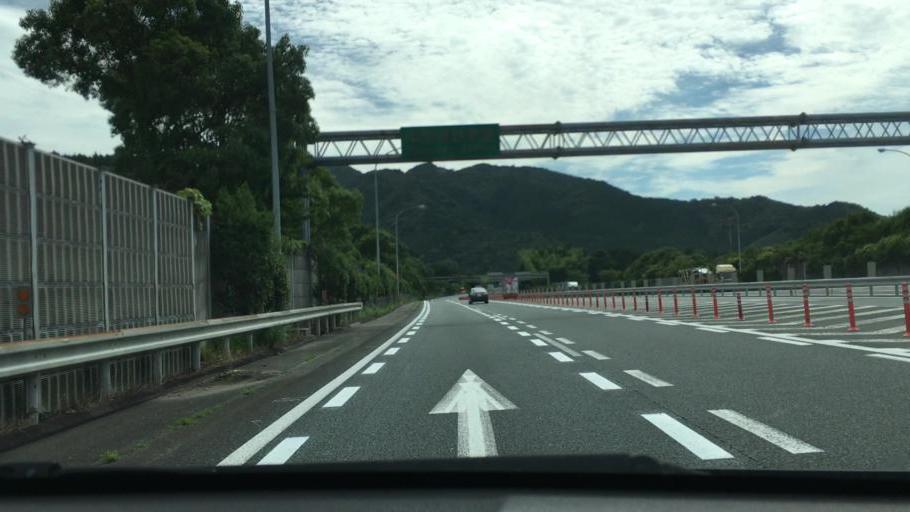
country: JP
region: Yamaguchi
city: Ogori-shimogo
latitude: 34.1315
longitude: 131.4464
